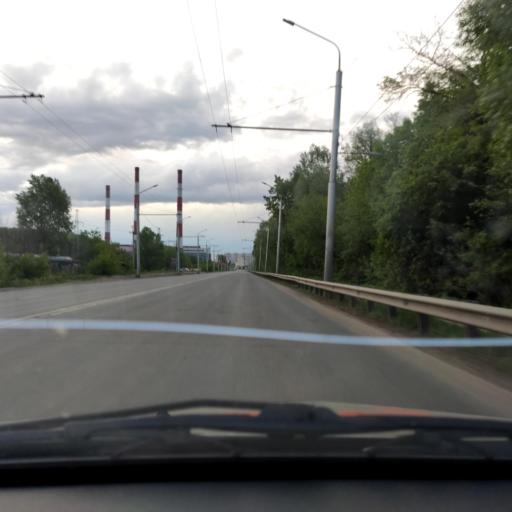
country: RU
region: Bashkortostan
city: Ufa
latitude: 54.7904
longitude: 56.1052
